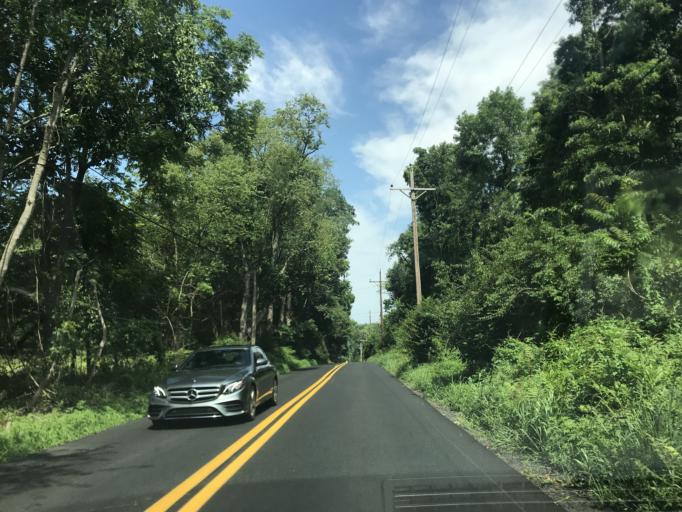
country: US
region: Delaware
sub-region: New Castle County
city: Greenville
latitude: 39.8197
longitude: -75.6033
